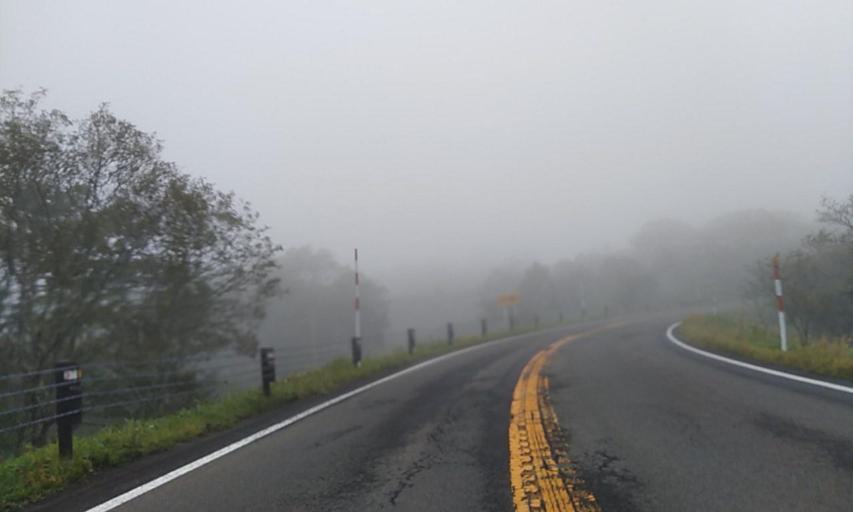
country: JP
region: Hokkaido
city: Bihoro
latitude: 43.5511
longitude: 144.5050
